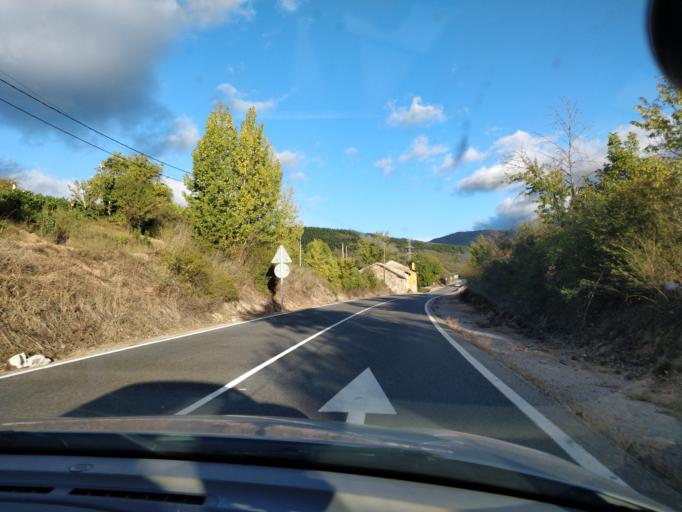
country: ES
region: Castille and Leon
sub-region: Provincia de Leon
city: Borrenes
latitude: 42.4997
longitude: -6.7274
